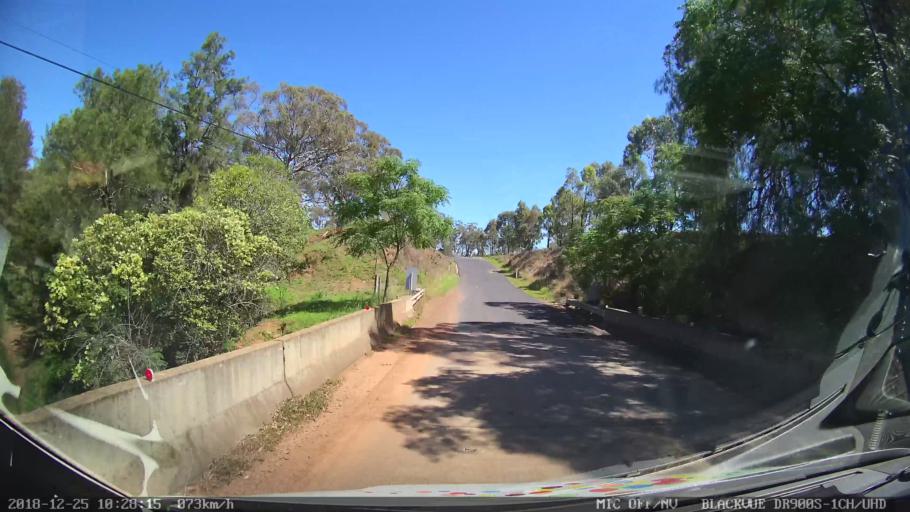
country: AU
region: New South Wales
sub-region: Muswellbrook
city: Denman
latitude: -32.3834
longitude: 150.4653
